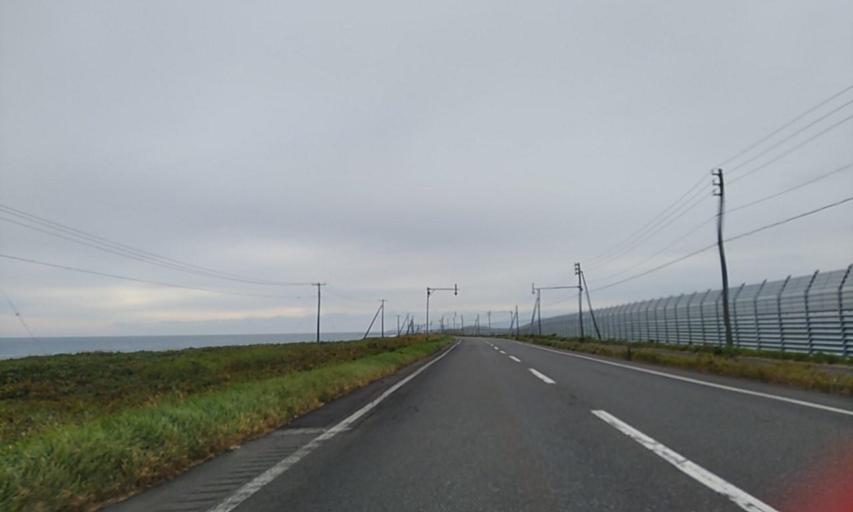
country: JP
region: Hokkaido
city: Makubetsu
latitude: 45.3202
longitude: 142.1856
